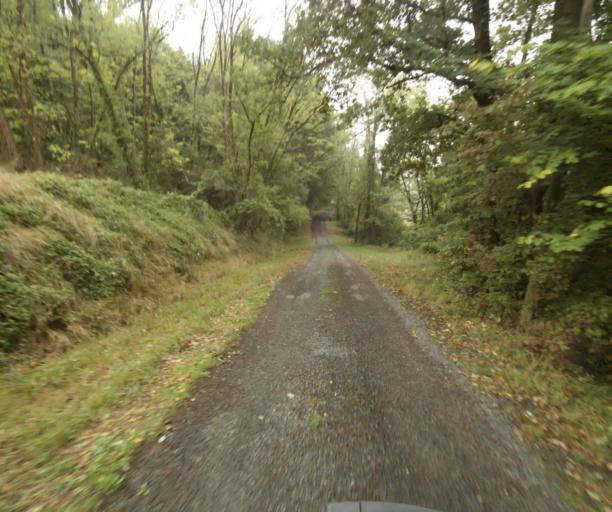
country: FR
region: Midi-Pyrenees
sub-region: Departement du Tarn-et-Garonne
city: Nohic
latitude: 43.8958
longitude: 1.4756
